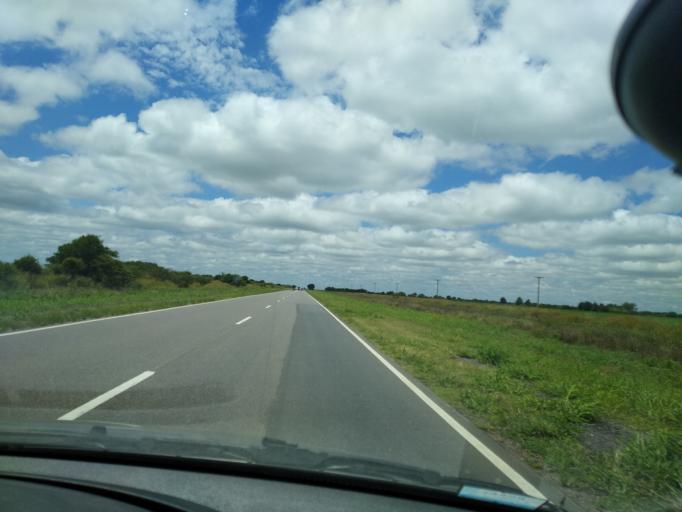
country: AR
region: Cordoba
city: Toledo
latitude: -31.6448
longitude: -64.0016
